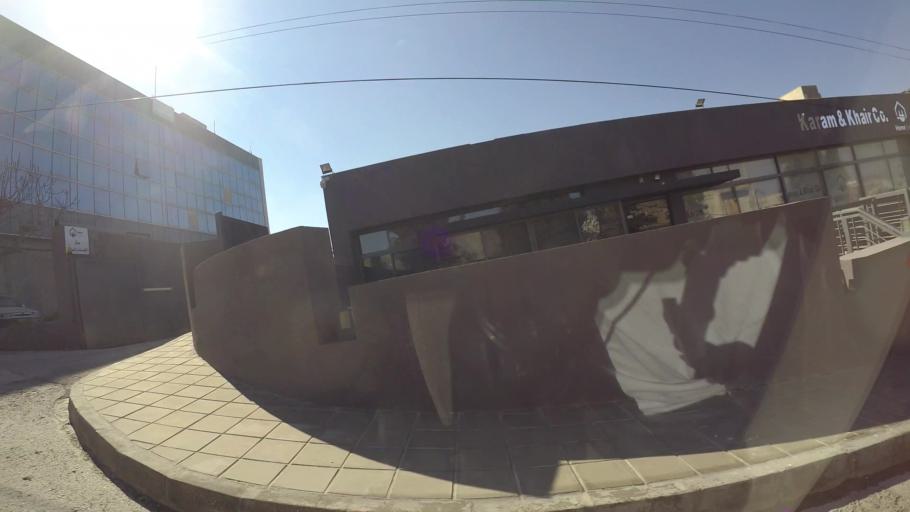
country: JO
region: Amman
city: Al Bunayyat ash Shamaliyah
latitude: 31.9137
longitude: 35.9038
